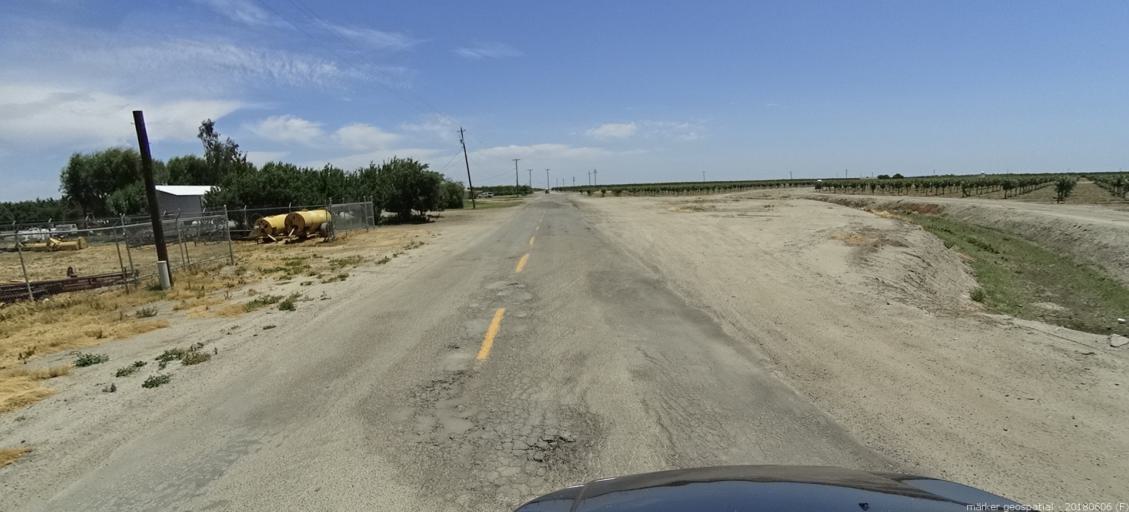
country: US
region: California
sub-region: Fresno County
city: Firebaugh
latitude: 36.8367
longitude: -120.3865
